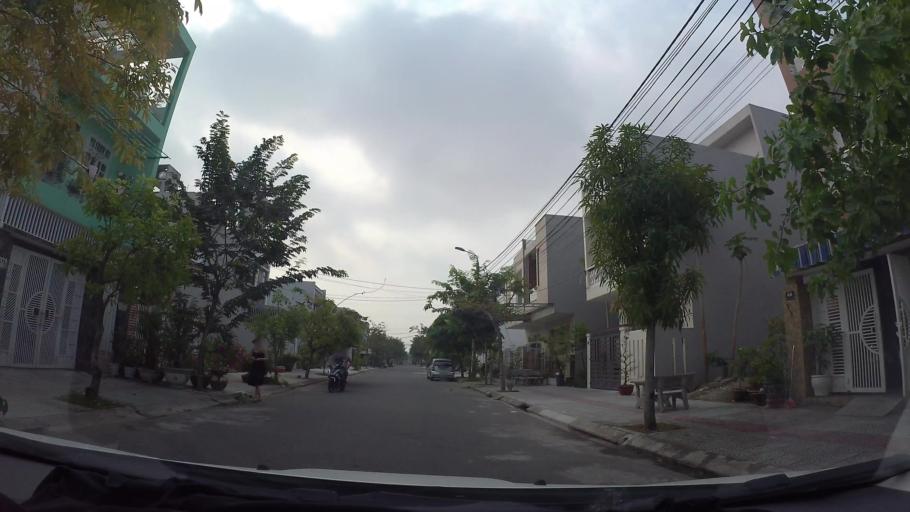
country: VN
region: Da Nang
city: Cam Le
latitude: 16.0088
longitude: 108.2174
